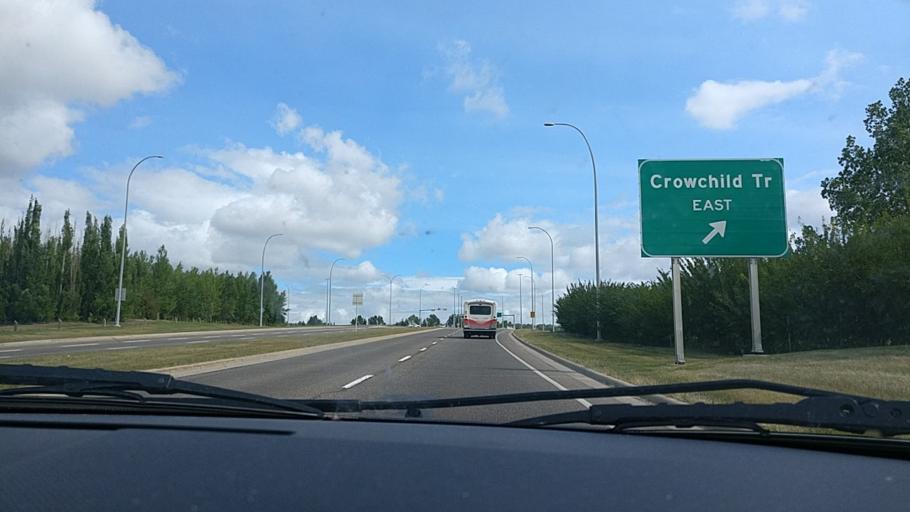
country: CA
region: Alberta
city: Calgary
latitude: 51.1073
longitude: -114.1803
